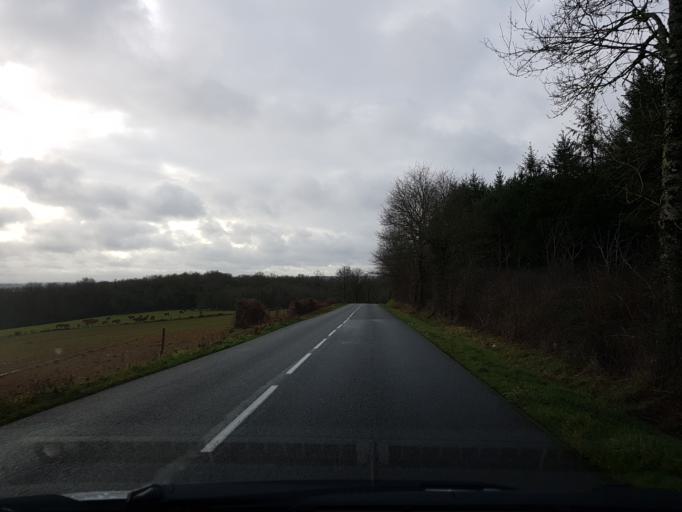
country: FR
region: Poitou-Charentes
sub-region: Departement de la Charente
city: Chabanais
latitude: 45.9066
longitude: 0.7334
